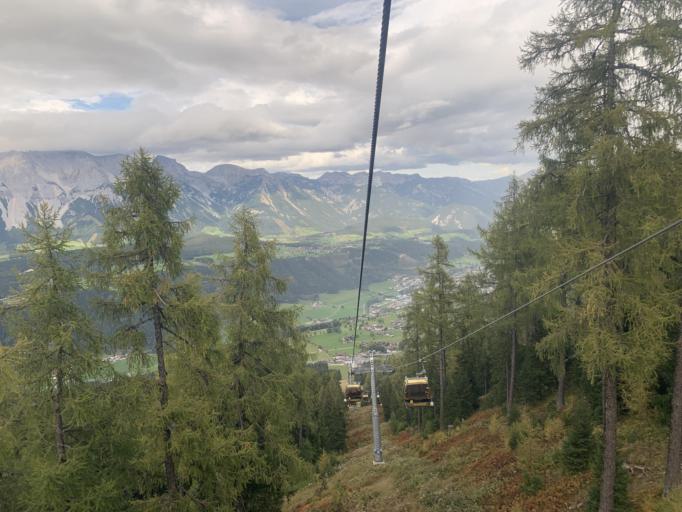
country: AT
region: Styria
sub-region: Politischer Bezirk Liezen
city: Schladming
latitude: 47.3641
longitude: 13.6428
